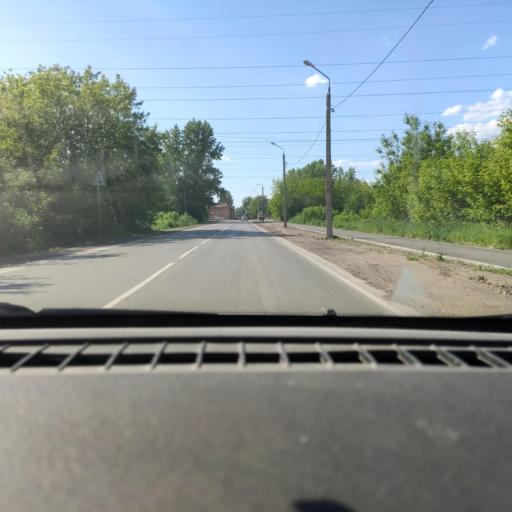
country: RU
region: Perm
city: Krasnokamsk
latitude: 58.0762
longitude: 55.7791
